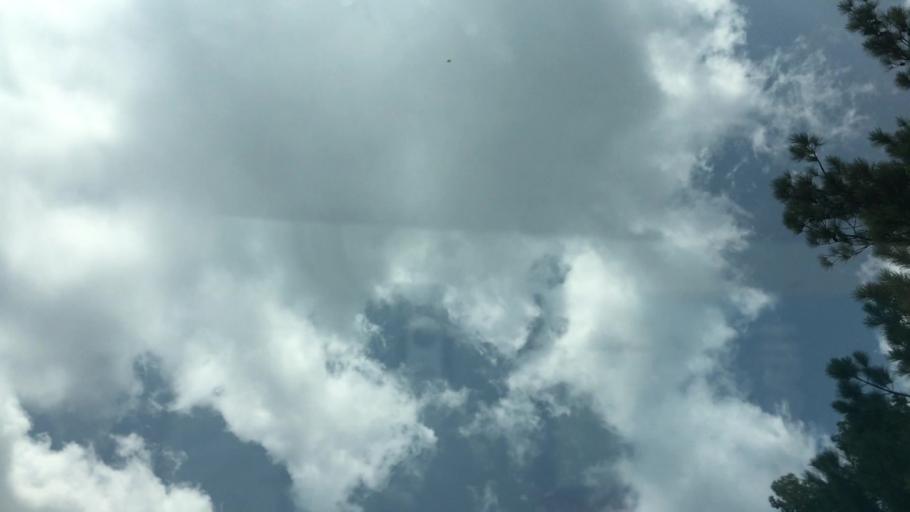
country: US
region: Alabama
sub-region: Pickens County
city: Gordo
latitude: 33.2820
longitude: -87.8102
